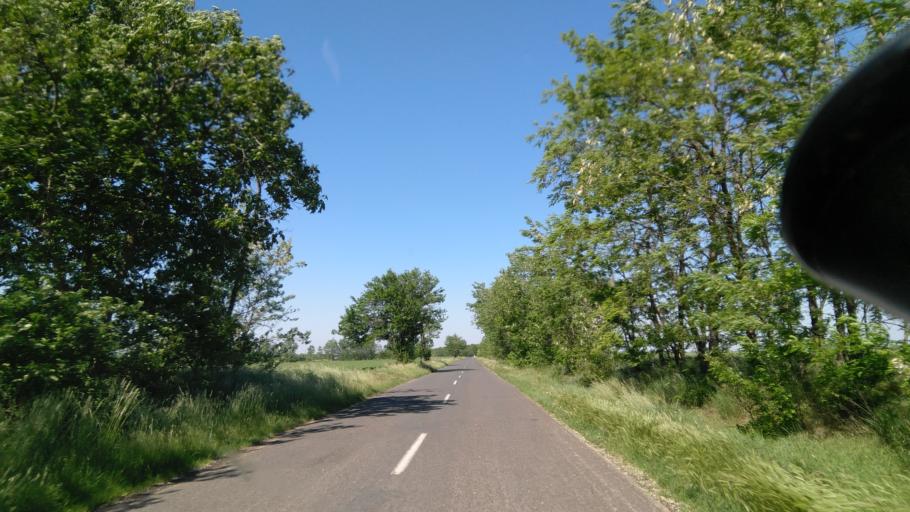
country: HU
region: Bekes
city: Kevermes
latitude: 46.4252
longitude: 21.1401
